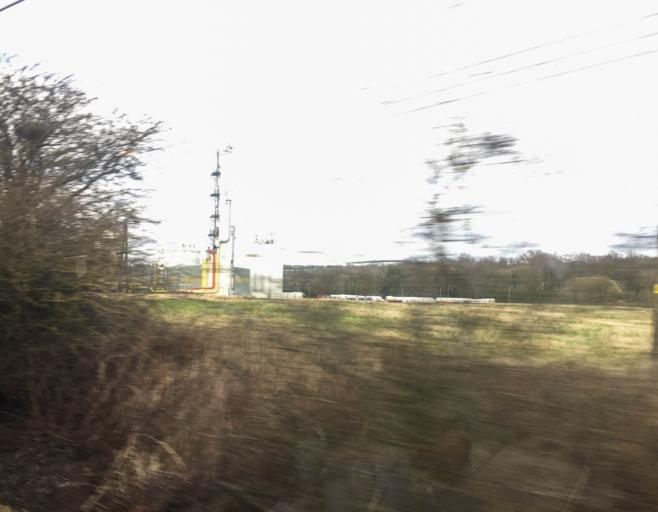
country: GB
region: Scotland
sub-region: North Lanarkshire
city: Newarthill
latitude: 55.7994
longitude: -3.9533
